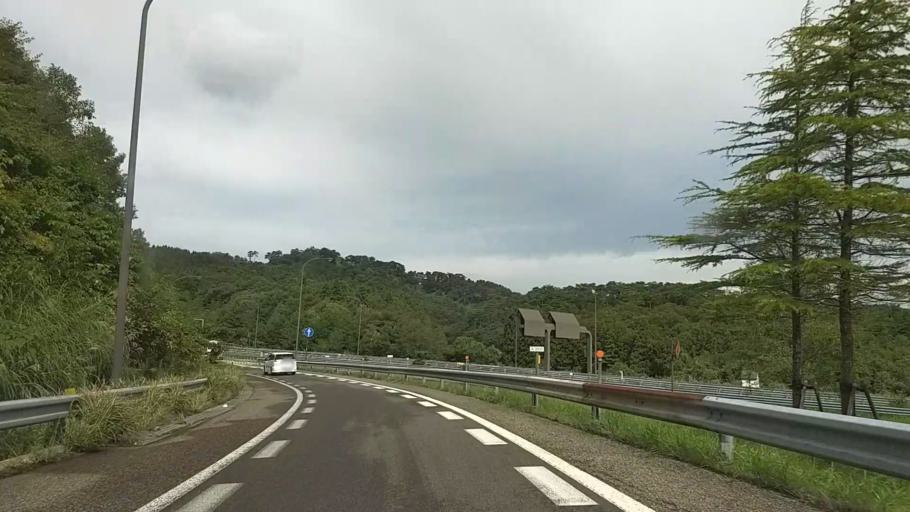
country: JP
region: Niigata
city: Joetsu
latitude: 37.1394
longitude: 138.2139
